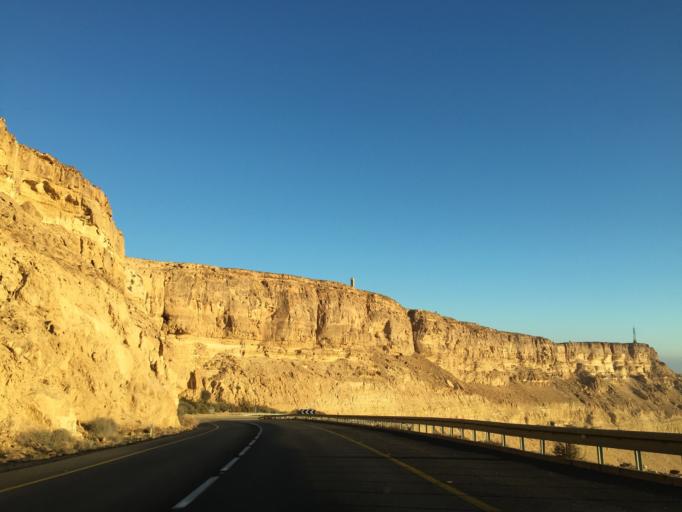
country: IL
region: Southern District
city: Mitzpe Ramon
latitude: 30.6148
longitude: 34.8092
